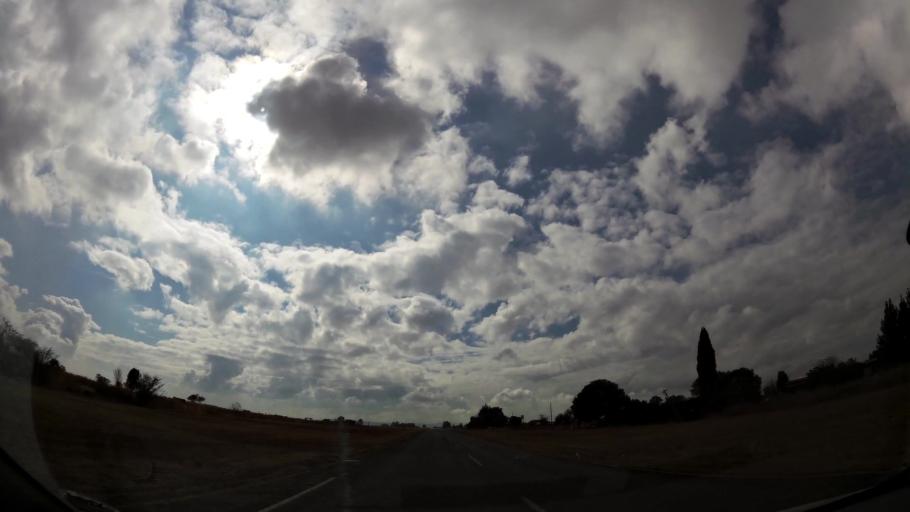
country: ZA
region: Gauteng
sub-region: Sedibeng District Municipality
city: Meyerton
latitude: -26.6157
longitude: 28.0621
